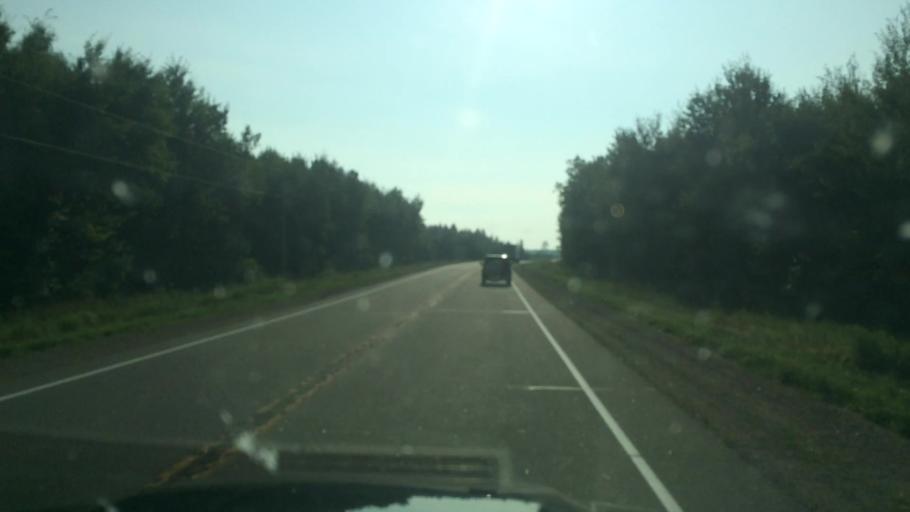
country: US
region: Wisconsin
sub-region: Lincoln County
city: Merrill
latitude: 45.1482
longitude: -89.4201
